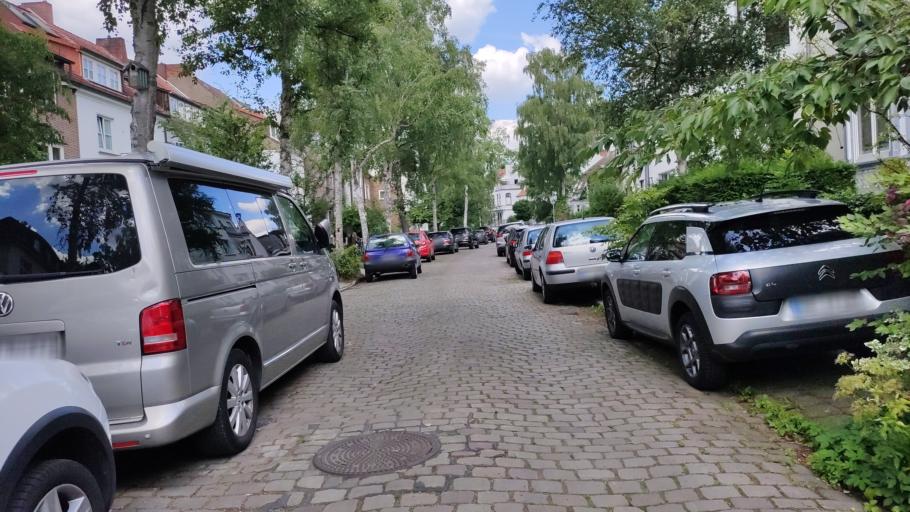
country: DE
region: Bremen
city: Bremen
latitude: 53.0845
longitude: 8.8427
